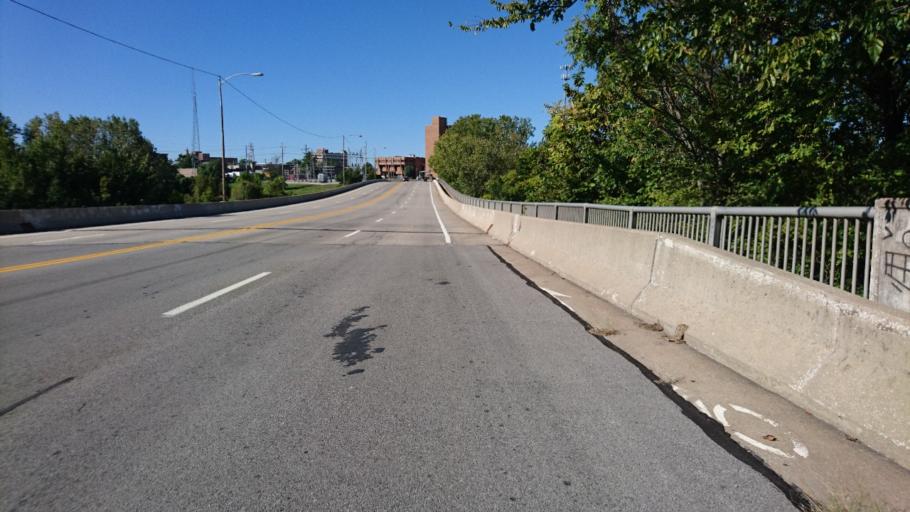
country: US
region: Missouri
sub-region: Jasper County
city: Joplin
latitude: 37.0916
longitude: -94.5088
